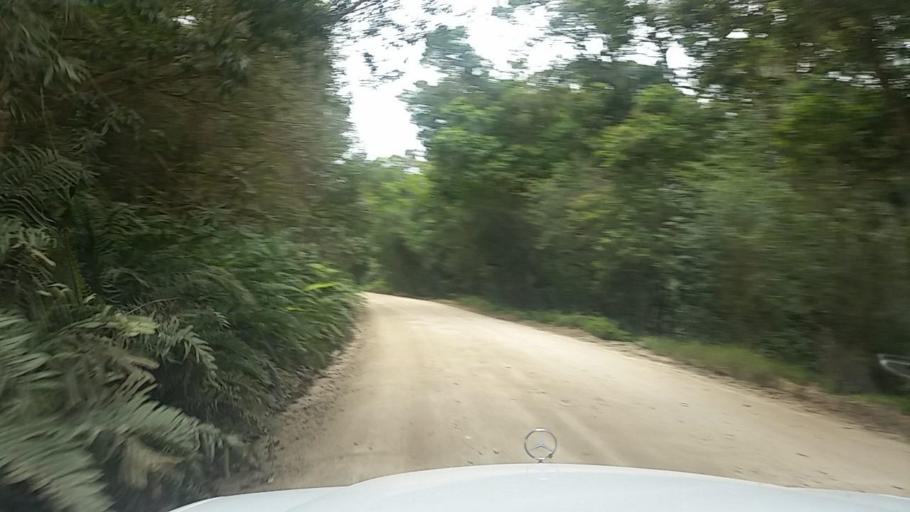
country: ZA
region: Western Cape
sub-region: Eden District Municipality
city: Knysna
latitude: -33.9547
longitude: 23.1488
